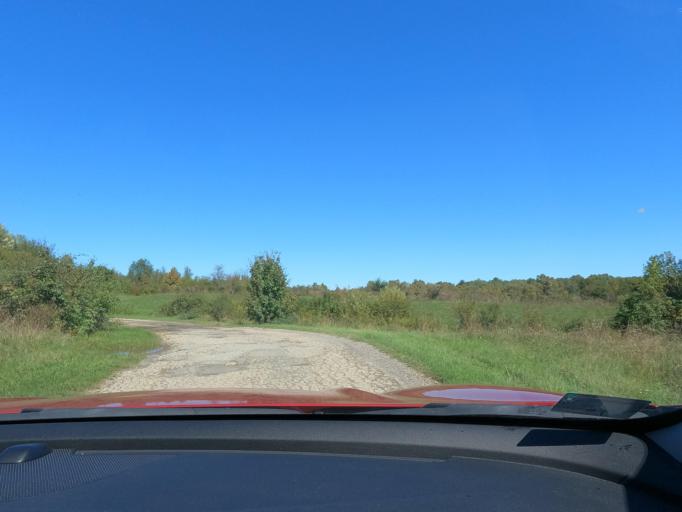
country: HR
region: Sisacko-Moslavacka
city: Petrinja
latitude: 45.3367
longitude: 16.2174
